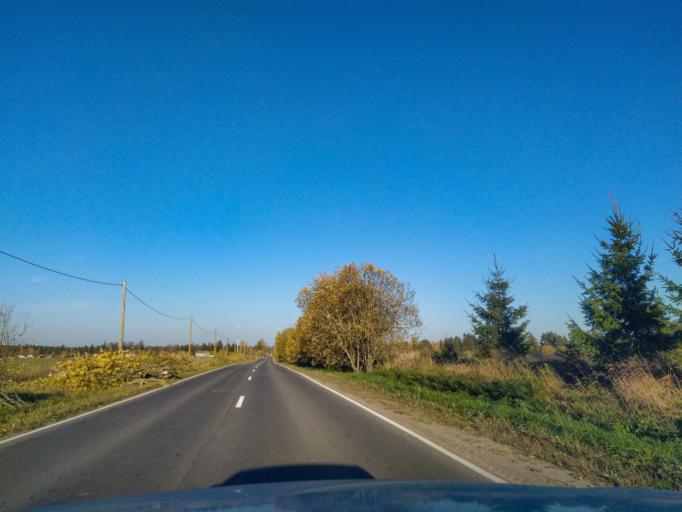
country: RU
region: Leningrad
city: Siverskiy
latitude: 59.3304
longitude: 30.0455
